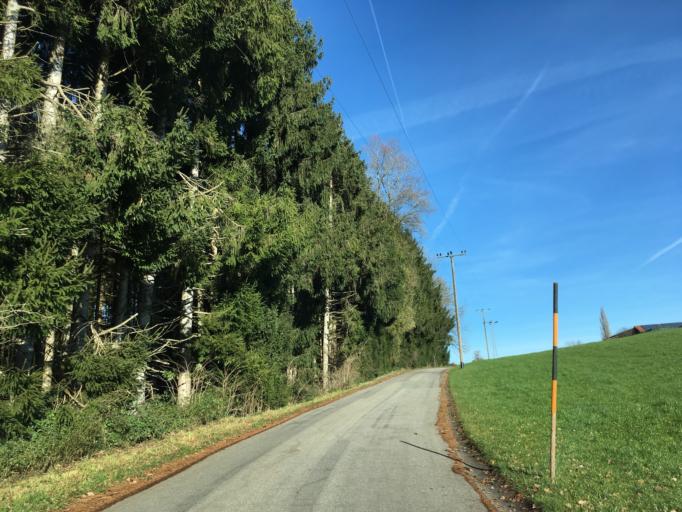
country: DE
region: Bavaria
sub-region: Upper Bavaria
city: Prutting
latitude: 47.9132
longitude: 12.1916
